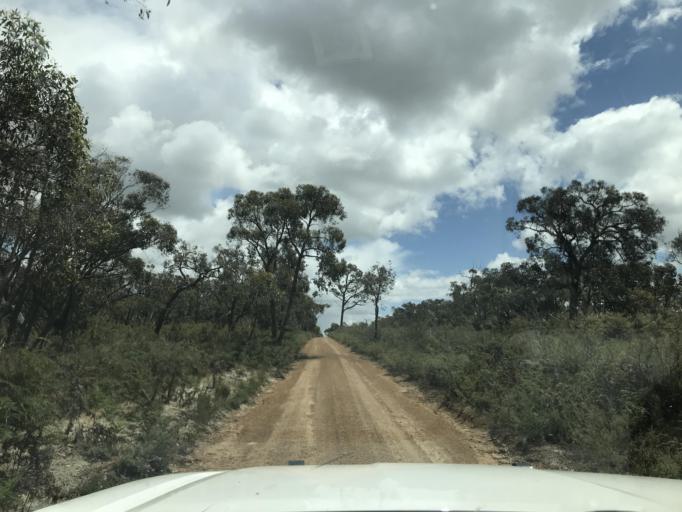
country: AU
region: South Australia
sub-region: Wattle Range
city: Penola
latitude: -37.0896
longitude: 141.3411
